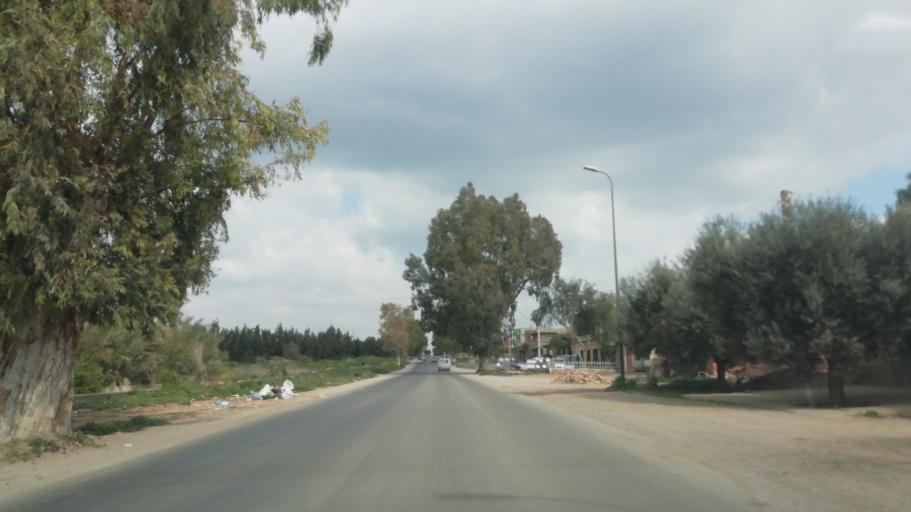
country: DZ
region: Mascara
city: Mascara
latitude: 35.6266
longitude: 0.1240
